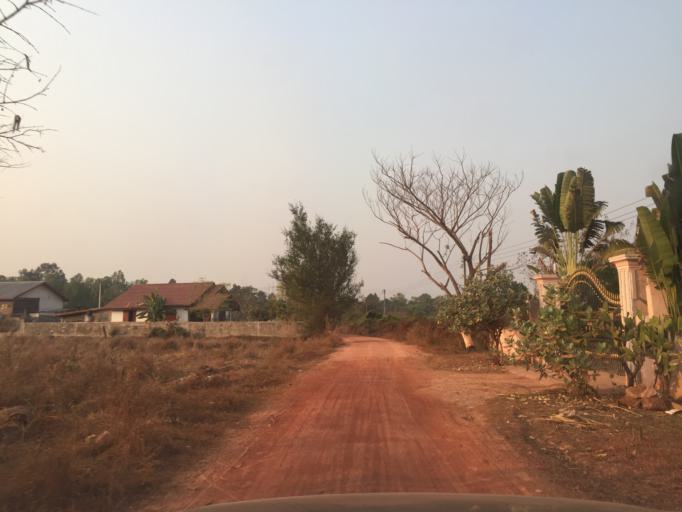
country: LA
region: Vientiane
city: Vientiane
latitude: 18.0593
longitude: 102.5209
